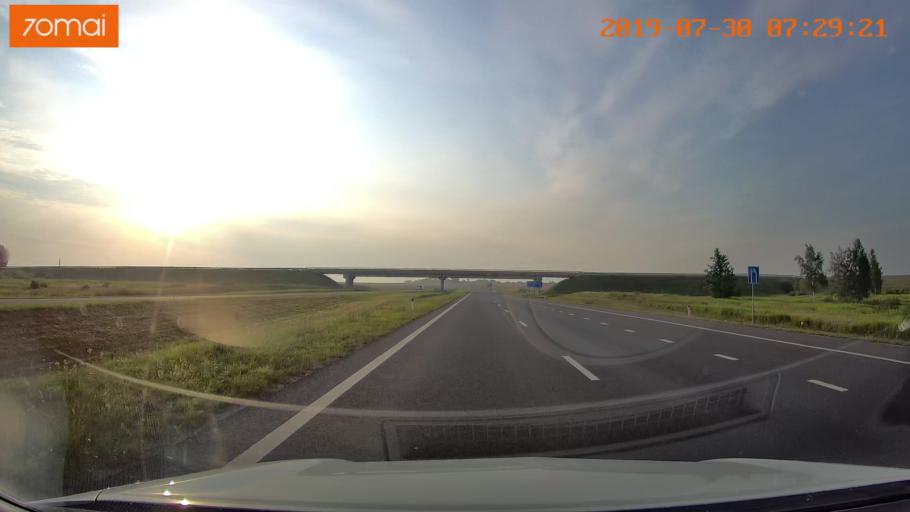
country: RU
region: Kaliningrad
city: Gvardeysk
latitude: 54.6727
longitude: 20.9371
